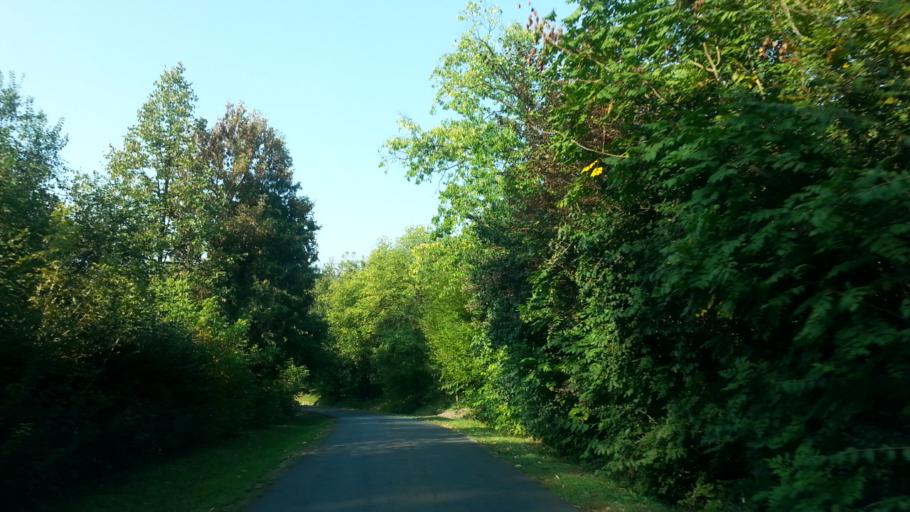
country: RS
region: Central Serbia
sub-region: Belgrade
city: Savski Venac
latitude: 44.7832
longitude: 20.4423
